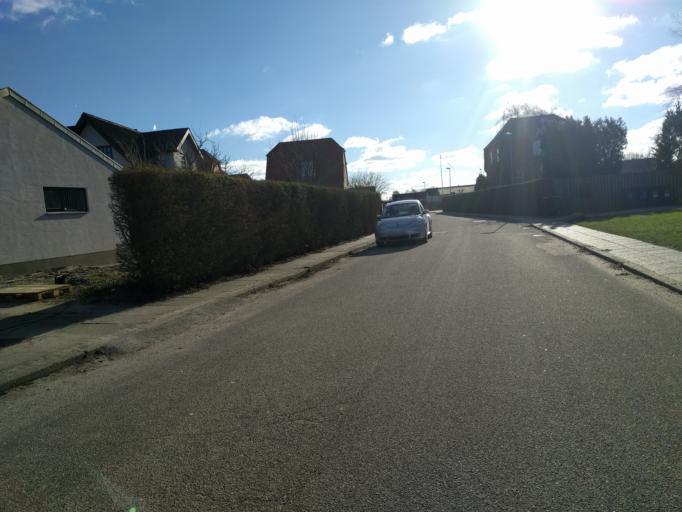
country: DK
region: North Denmark
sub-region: Alborg Kommune
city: Aalborg
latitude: 57.0301
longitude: 9.9202
